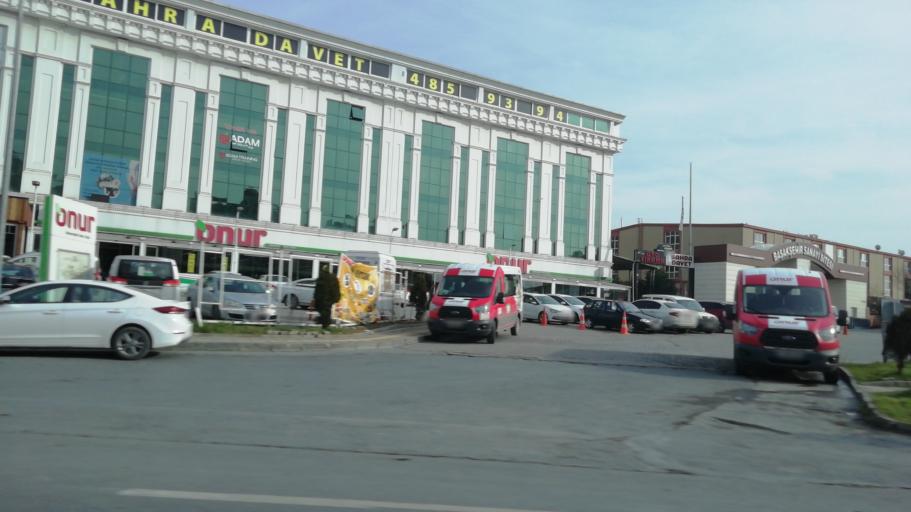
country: TR
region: Istanbul
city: Basaksehir
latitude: 41.1020
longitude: 28.7934
